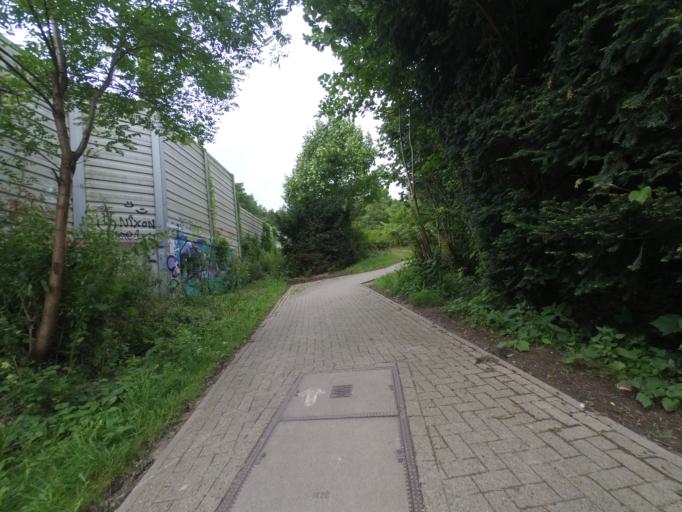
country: DE
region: Hamburg
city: Marienthal
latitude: 53.5537
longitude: 10.0679
